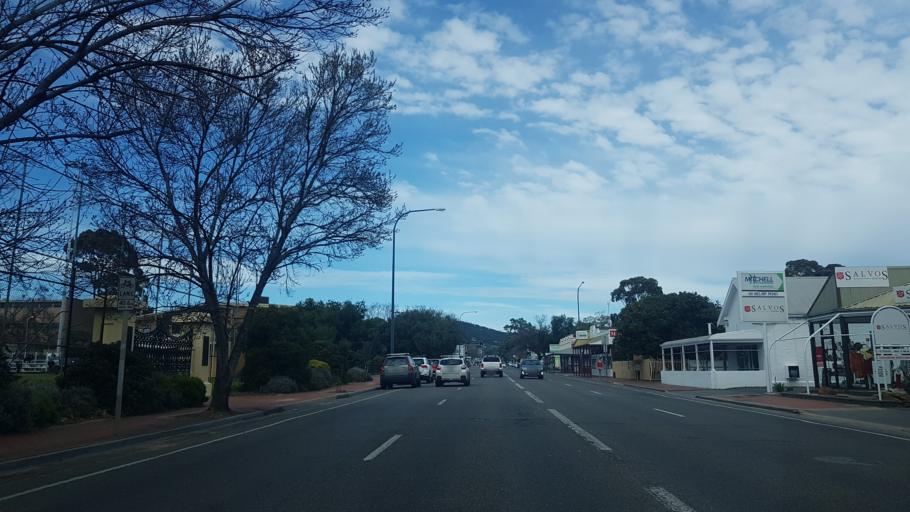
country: AU
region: South Australia
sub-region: Unley
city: Unley Park
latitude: -34.9684
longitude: 138.6089
